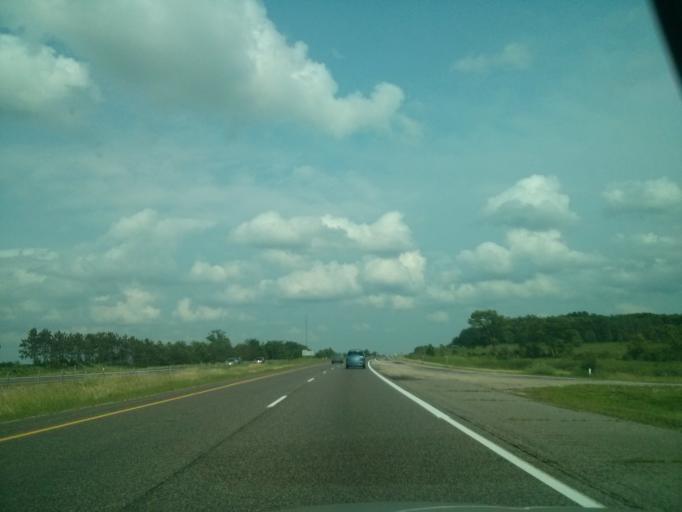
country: US
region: Wisconsin
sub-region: Saint Croix County
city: Hammond
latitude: 44.9422
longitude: -92.4338
